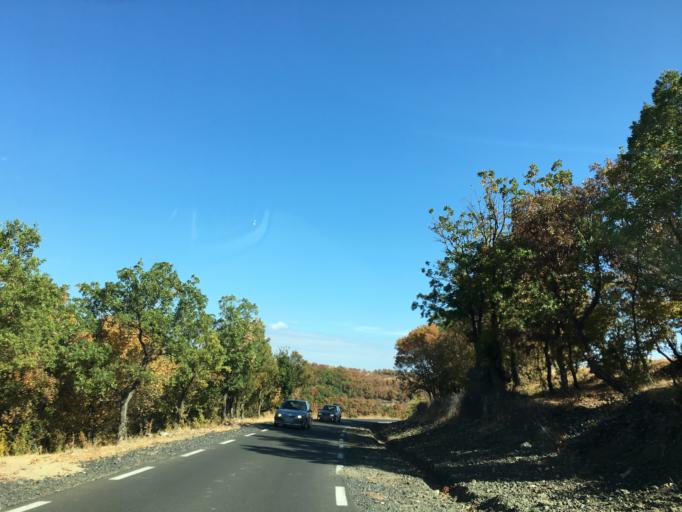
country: BG
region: Kurdzhali
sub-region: Obshtina Krumovgrad
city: Krumovgrad
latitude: 41.4832
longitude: 25.5222
